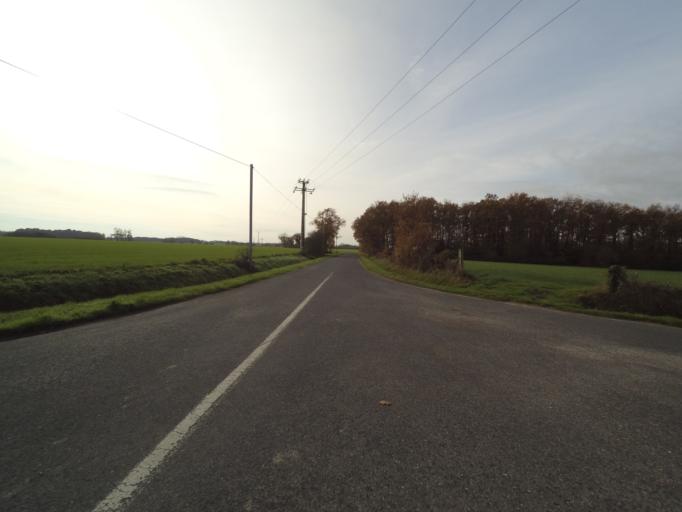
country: FR
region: Pays de la Loire
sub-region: Departement de la Loire-Atlantique
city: La Planche
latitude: 47.0007
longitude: -1.3948
